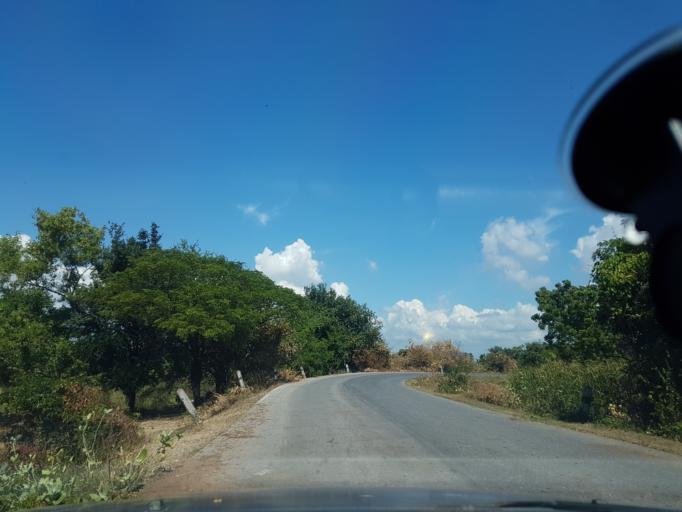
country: TH
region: Lop Buri
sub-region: Amphoe Tha Luang
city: Tha Luang
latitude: 14.9986
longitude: 101.0086
